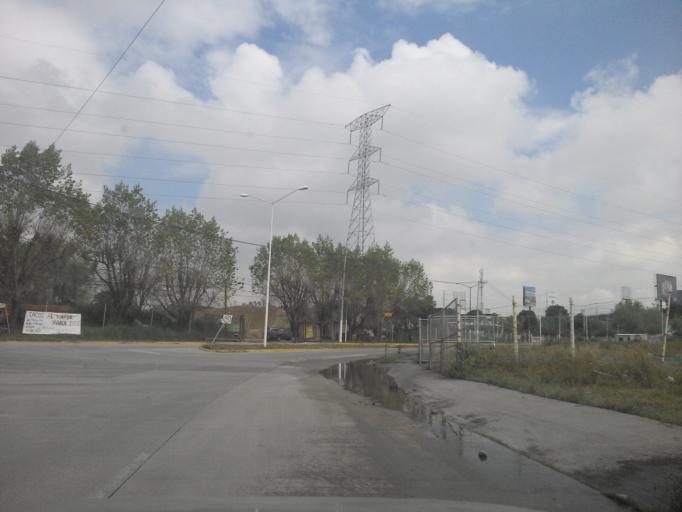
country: MX
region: Jalisco
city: Nuevo Mexico
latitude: 20.6985
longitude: -103.4621
